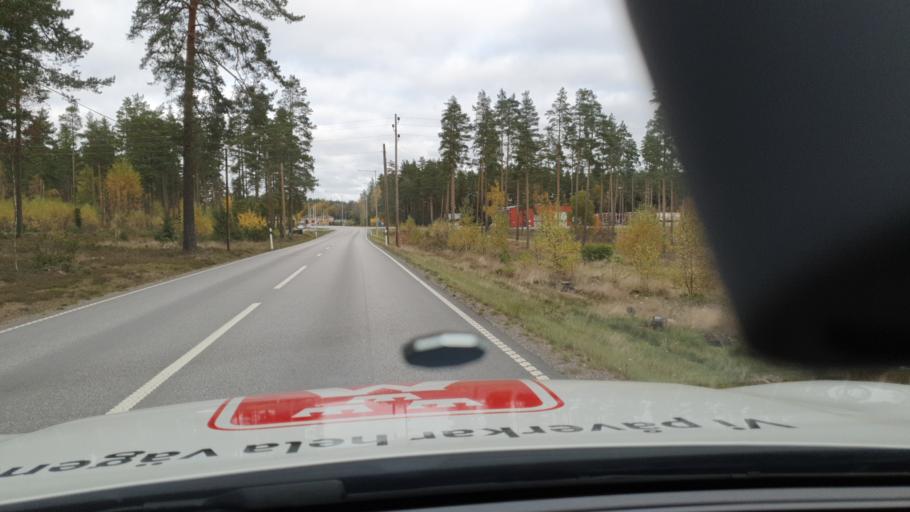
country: SE
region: OErebro
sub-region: Hallsbergs Kommun
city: Palsboda
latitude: 58.8907
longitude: 15.4296
